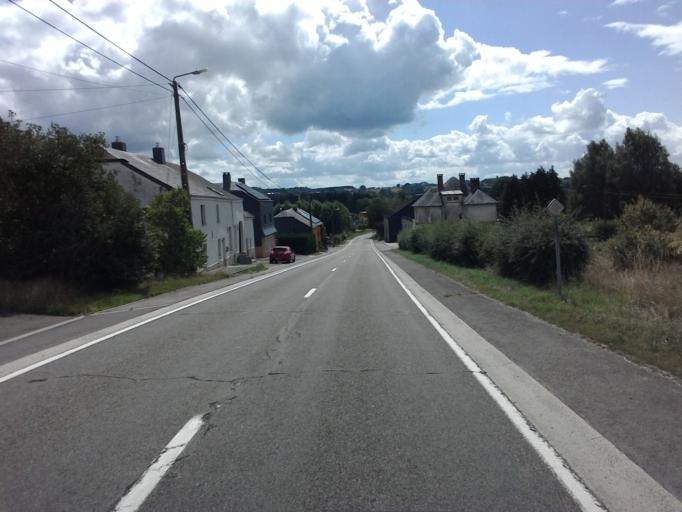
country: BE
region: Wallonia
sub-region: Province du Luxembourg
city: Habay-la-Vieille
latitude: 49.7843
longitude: 5.6044
